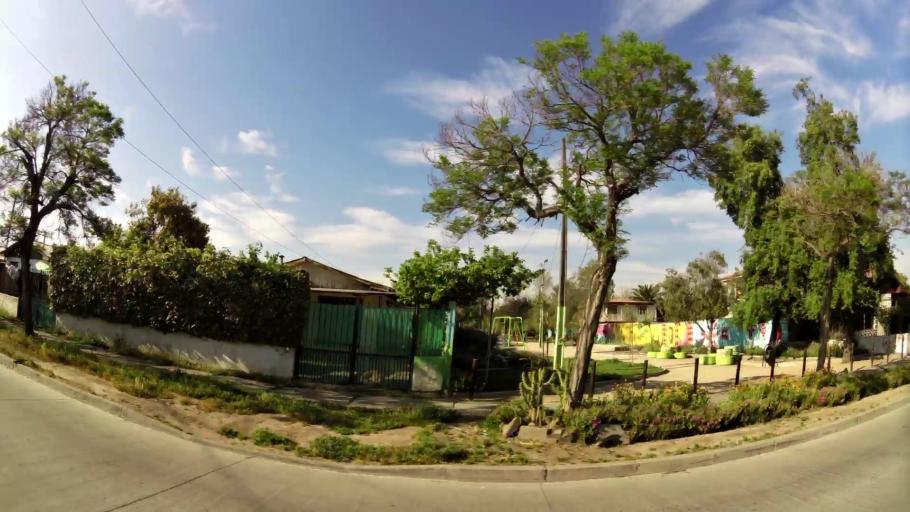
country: CL
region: Santiago Metropolitan
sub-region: Provincia de Santiago
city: La Pintana
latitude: -33.5628
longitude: -70.5893
